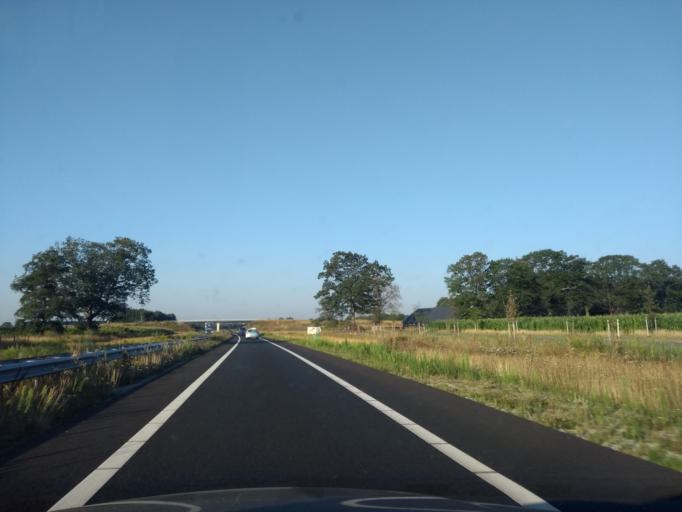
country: NL
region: Overijssel
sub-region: Gemeente Haaksbergen
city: Haaksbergen
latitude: 52.1729
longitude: 6.7148
